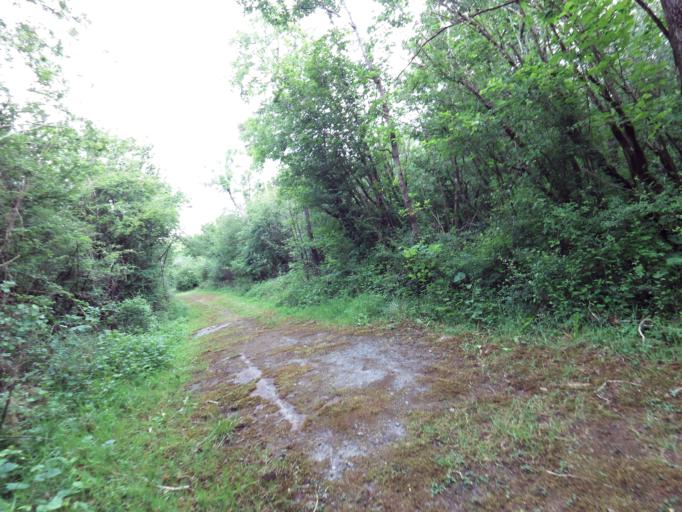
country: IE
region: Connaught
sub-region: County Galway
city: Gort
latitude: 53.0752
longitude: -8.8595
